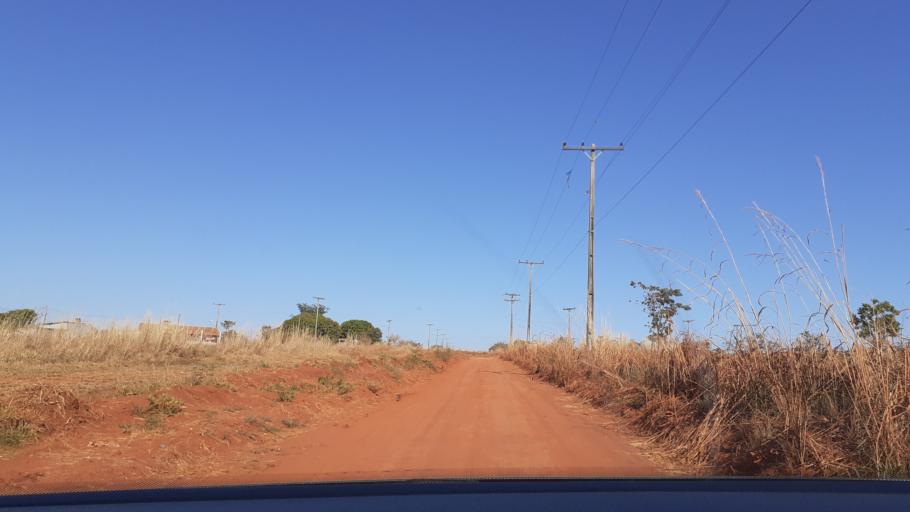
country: BR
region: Goias
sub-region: Aparecida De Goiania
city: Aparecida de Goiania
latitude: -16.8720
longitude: -49.2704
